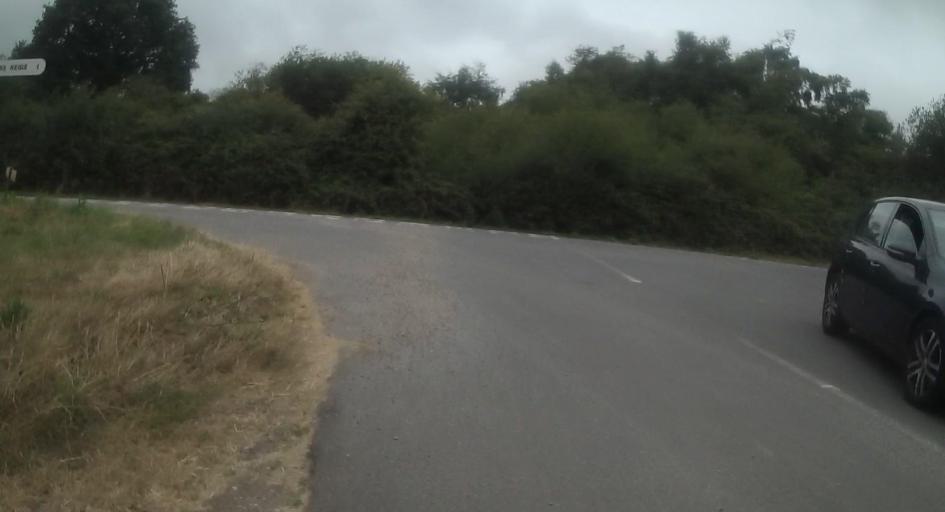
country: GB
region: England
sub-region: Dorset
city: Bovington Camp
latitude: 50.7398
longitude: -2.2191
